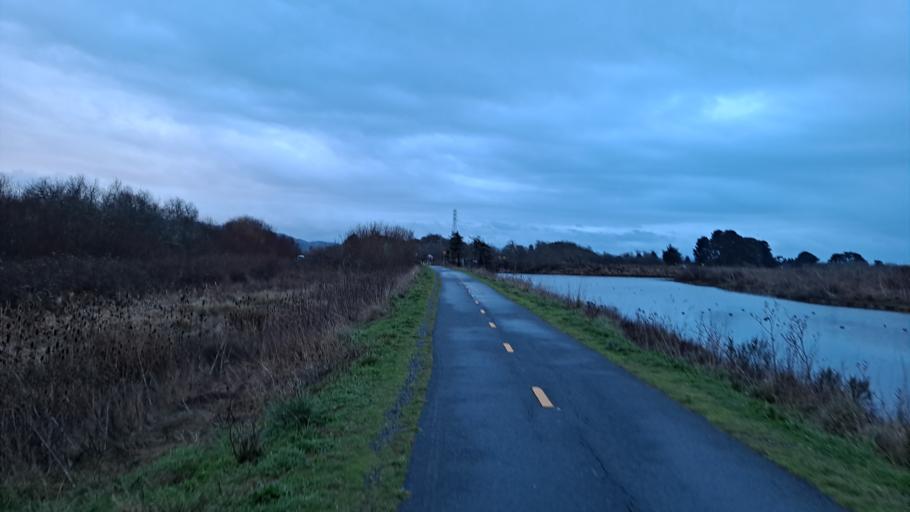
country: US
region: California
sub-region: Humboldt County
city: Arcata
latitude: 40.8627
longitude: -124.0934
